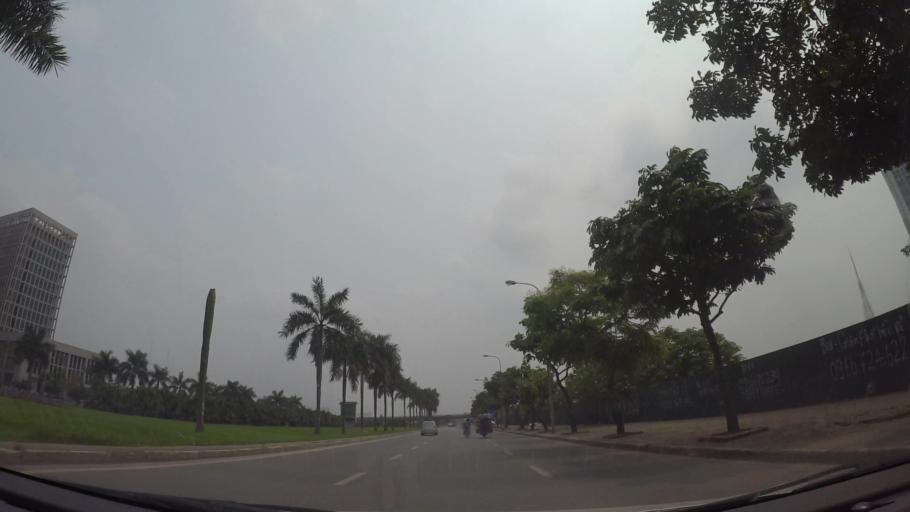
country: VN
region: Ha Noi
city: Thanh Xuan
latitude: 21.0067
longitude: 105.7734
